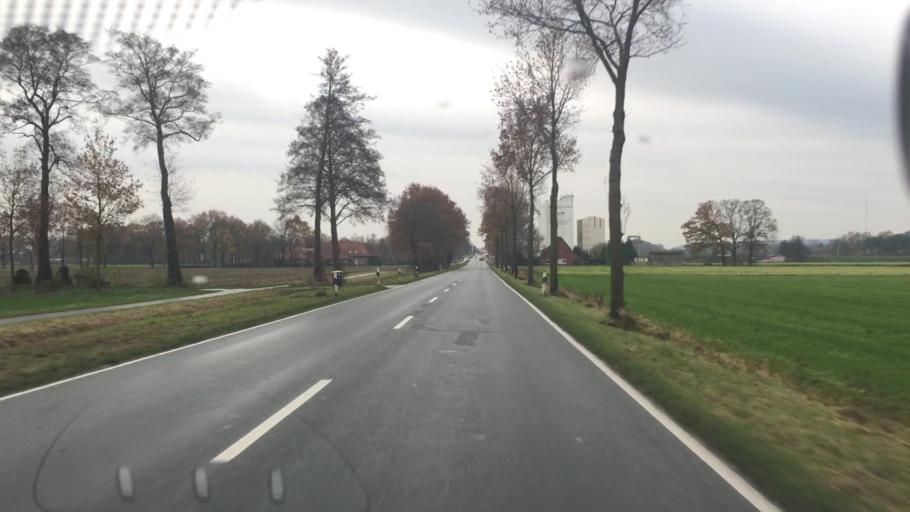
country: DE
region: Lower Saxony
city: Wallenhorst
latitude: 52.4150
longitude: 8.0605
